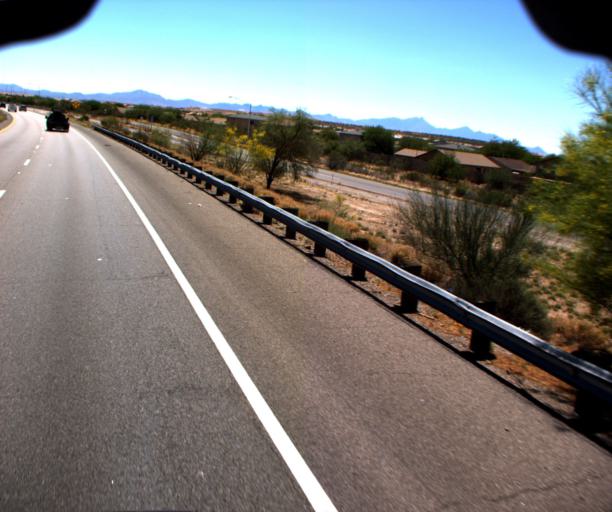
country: US
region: Arizona
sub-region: Pima County
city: Summit
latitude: 32.1333
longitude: -110.8871
